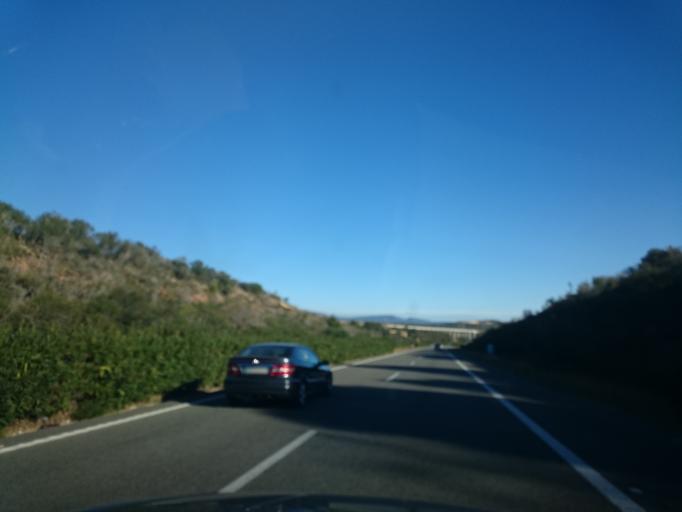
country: ES
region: Catalonia
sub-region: Provincia de Tarragona
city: Amposta
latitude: 40.7184
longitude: 0.5615
